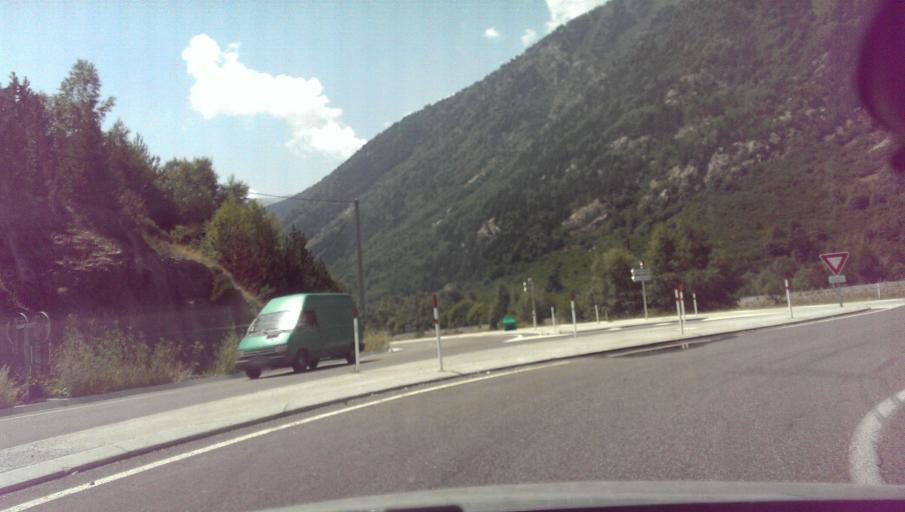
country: AD
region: Encamp
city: Pas de la Casa
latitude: 42.5368
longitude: 1.8242
